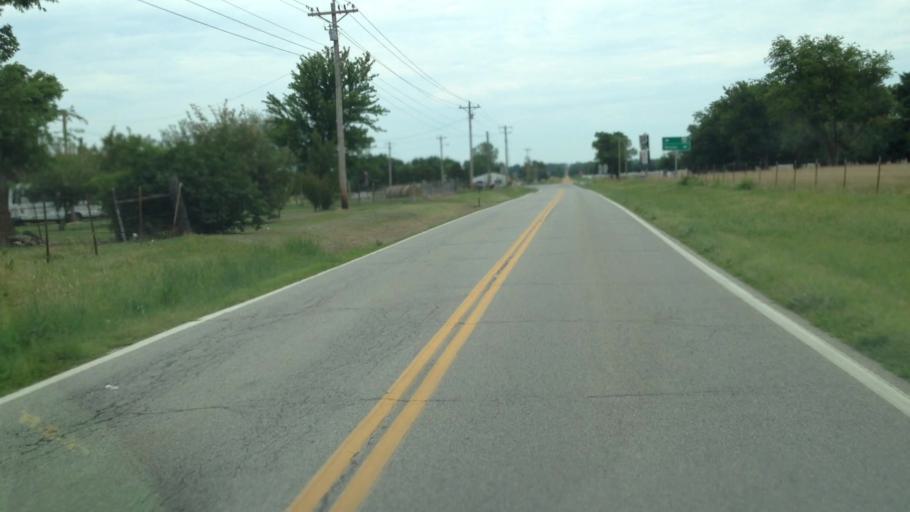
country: US
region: Oklahoma
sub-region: Delaware County
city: Cleora
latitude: 36.6106
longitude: -94.9634
